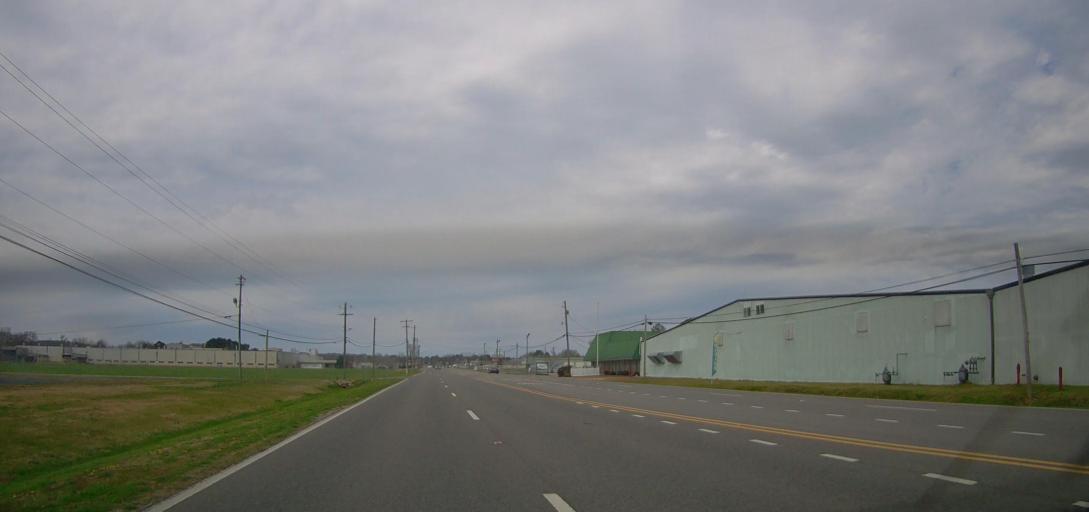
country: US
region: Alabama
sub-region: Marion County
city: Hamilton
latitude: 34.1099
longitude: -87.9893
